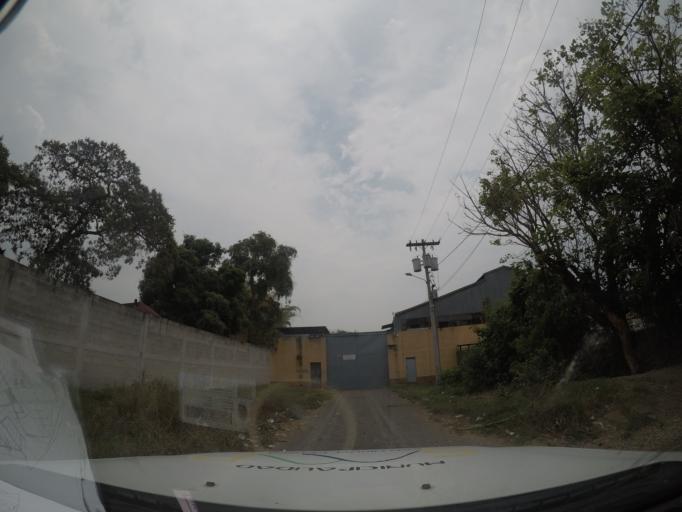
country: GT
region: Guatemala
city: Petapa
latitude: 14.5017
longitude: -90.5491
